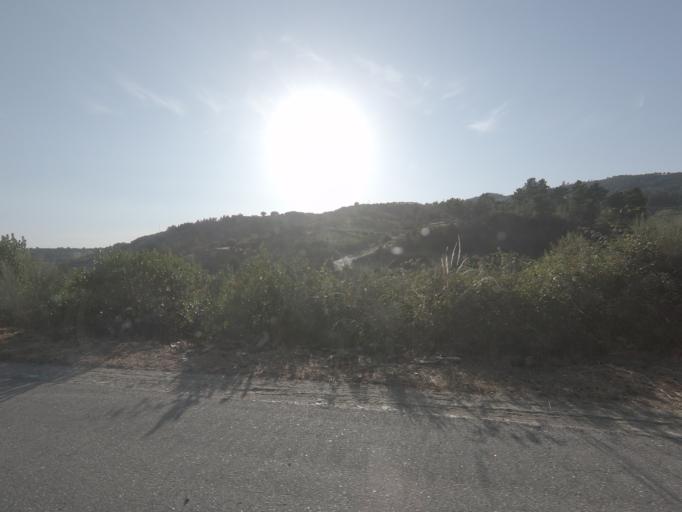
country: PT
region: Vila Real
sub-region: Sabrosa
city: Vilela
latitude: 41.1781
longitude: -7.5973
